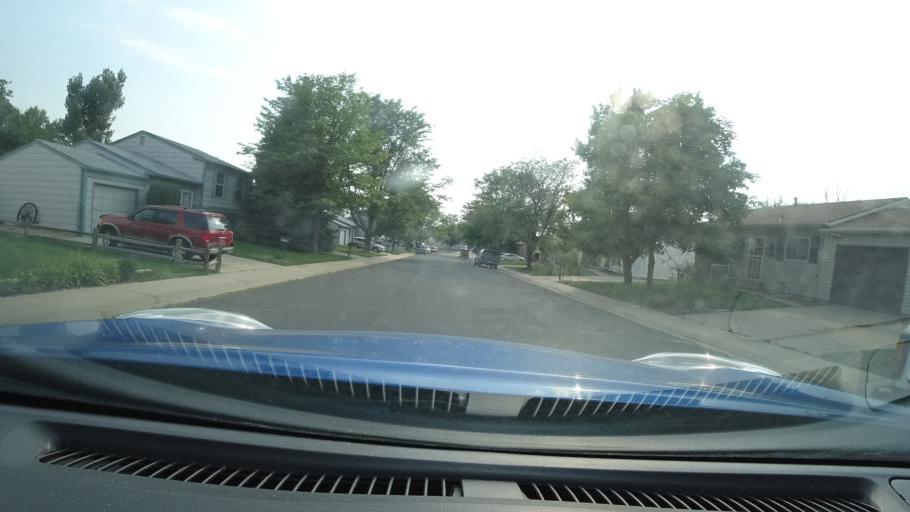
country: US
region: Colorado
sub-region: Adams County
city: Aurora
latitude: 39.7437
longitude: -104.7520
